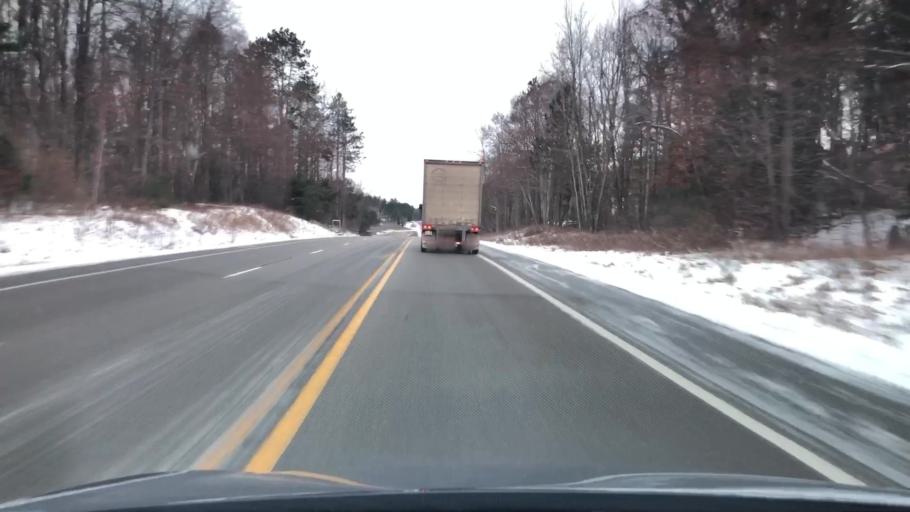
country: US
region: Michigan
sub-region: Wexford County
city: Cadillac
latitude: 44.1880
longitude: -85.3898
